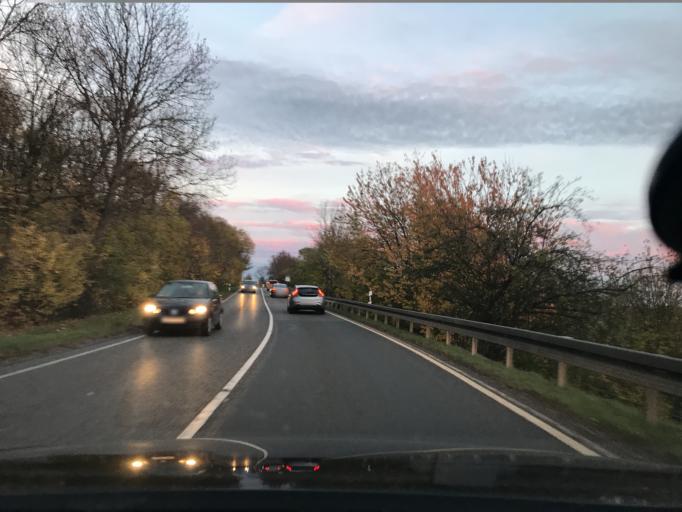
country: DE
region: Thuringia
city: Weimar
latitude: 50.9788
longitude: 11.2982
